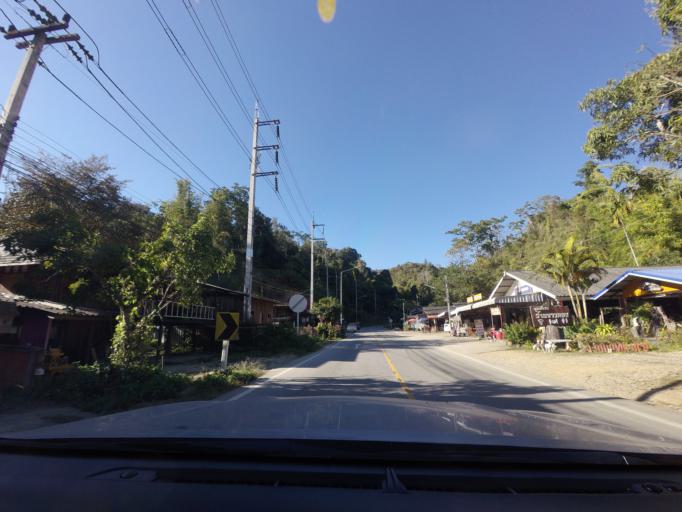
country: TH
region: Mae Hong Son
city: Mae Hi
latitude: 19.2047
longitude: 98.6706
